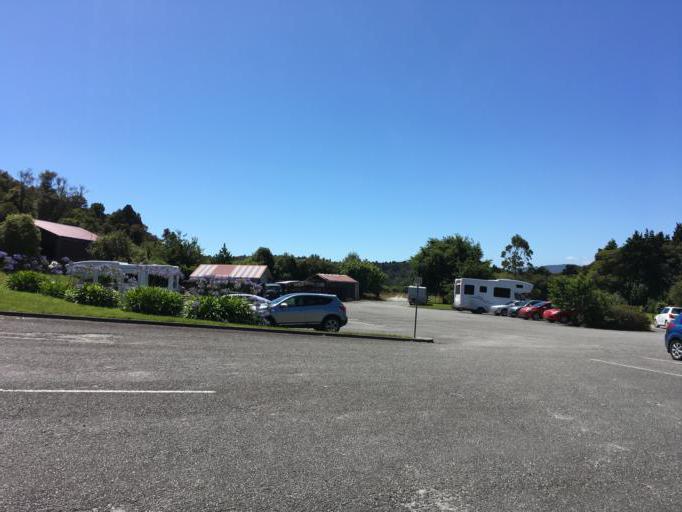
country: NZ
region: West Coast
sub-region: Grey District
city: Greymouth
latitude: -42.5349
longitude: 171.1821
